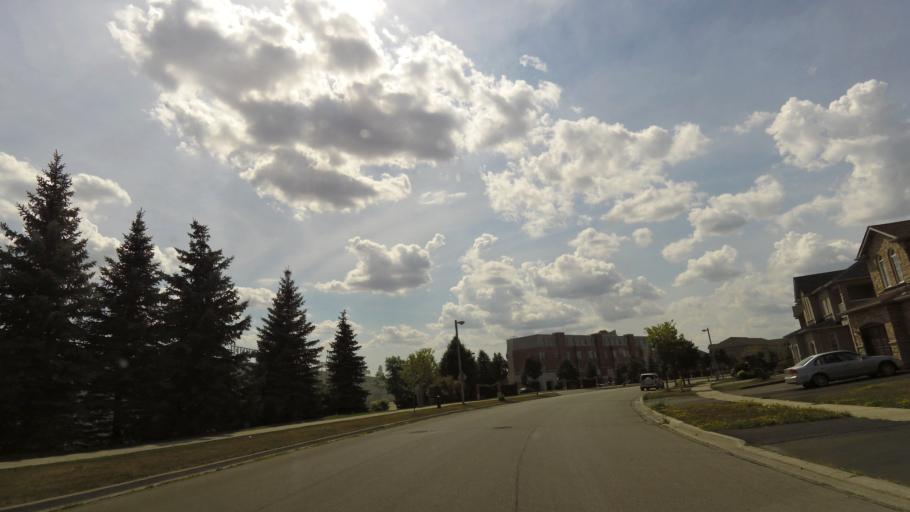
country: CA
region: Ontario
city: Vaughan
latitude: 43.7924
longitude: -79.5521
